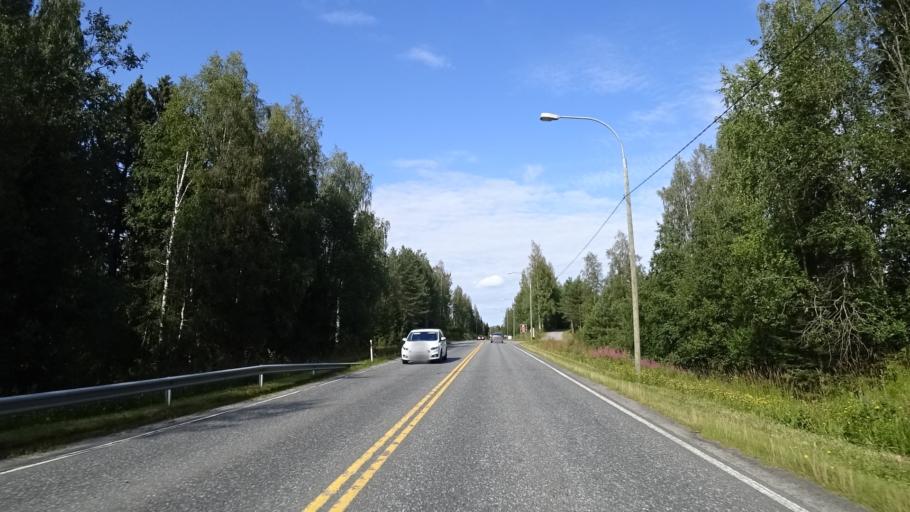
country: FI
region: North Karelia
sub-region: Joensuu
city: Eno
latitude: 62.7868
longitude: 30.0799
